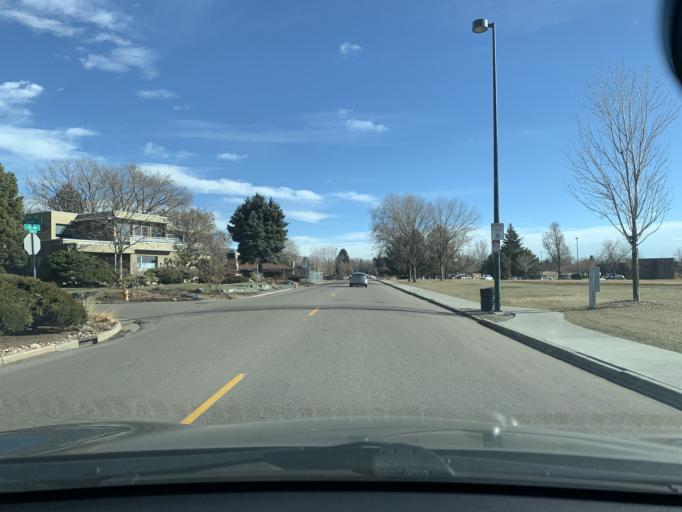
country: US
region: Colorado
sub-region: Jefferson County
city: Edgewater
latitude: 39.7530
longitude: -105.0502
